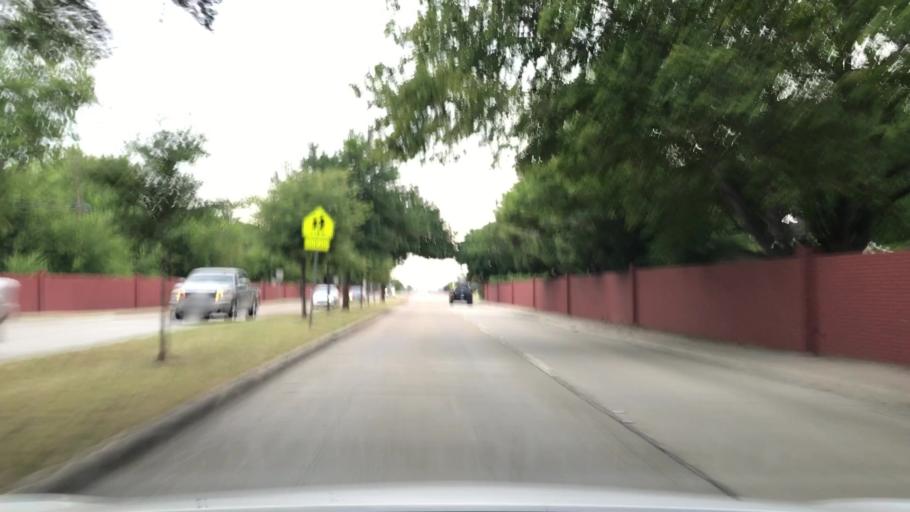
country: US
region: Texas
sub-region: Dallas County
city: Carrollton
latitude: 32.9684
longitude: -96.9048
